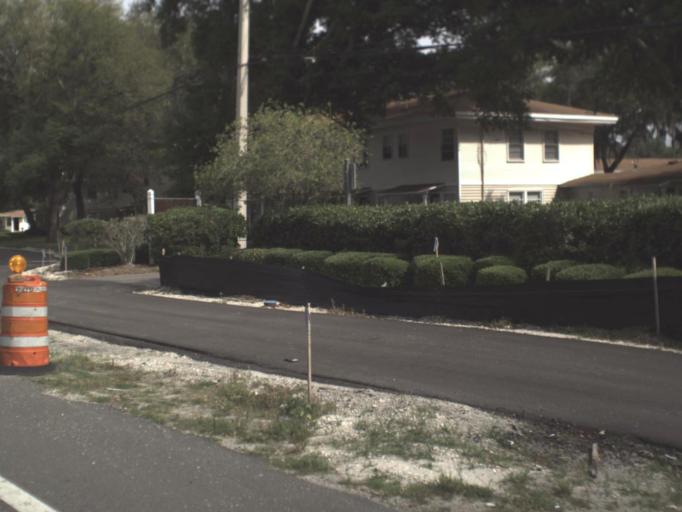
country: US
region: Florida
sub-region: Clay County
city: Green Cove Springs
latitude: 30.0090
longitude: -81.6960
